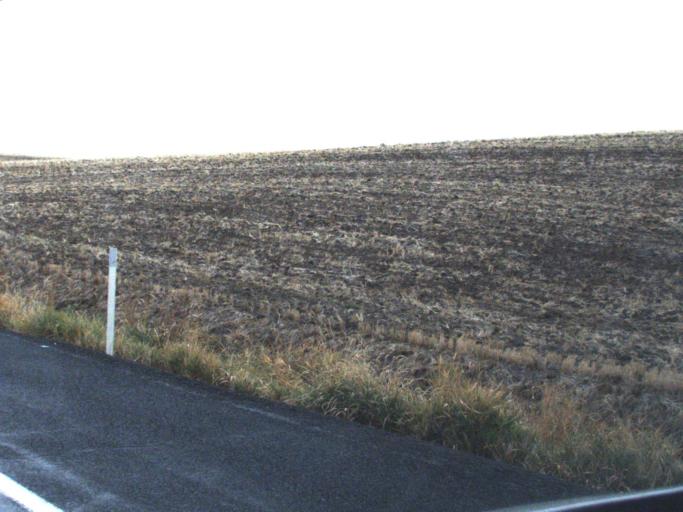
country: US
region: Washington
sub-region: Whitman County
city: Pullman
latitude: 46.6557
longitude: -117.1908
